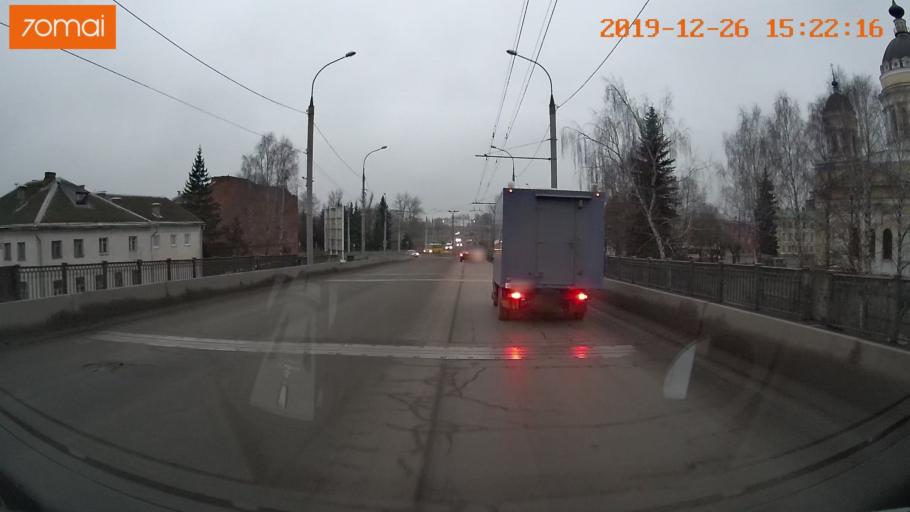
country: RU
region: Jaroslavl
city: Rybinsk
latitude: 58.0486
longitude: 38.8604
